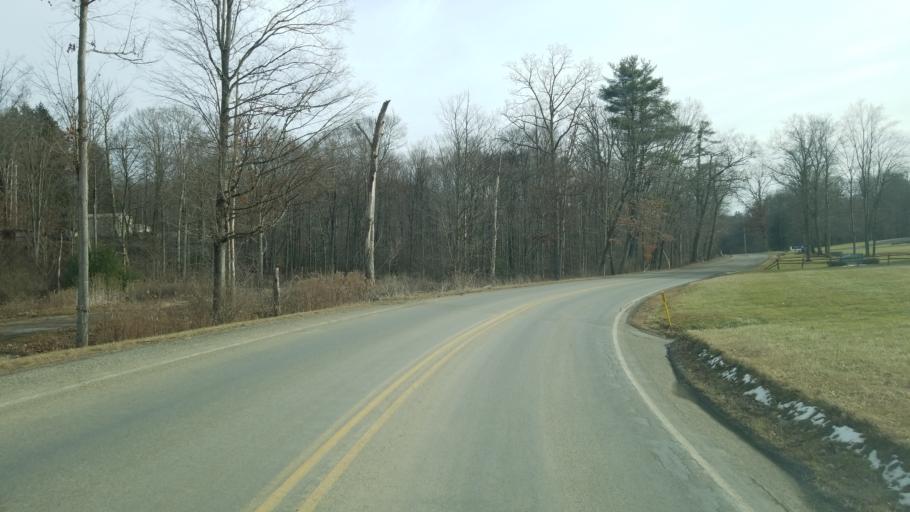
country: US
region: Pennsylvania
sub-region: Jefferson County
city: Punxsutawney
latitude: 40.9711
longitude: -79.0115
